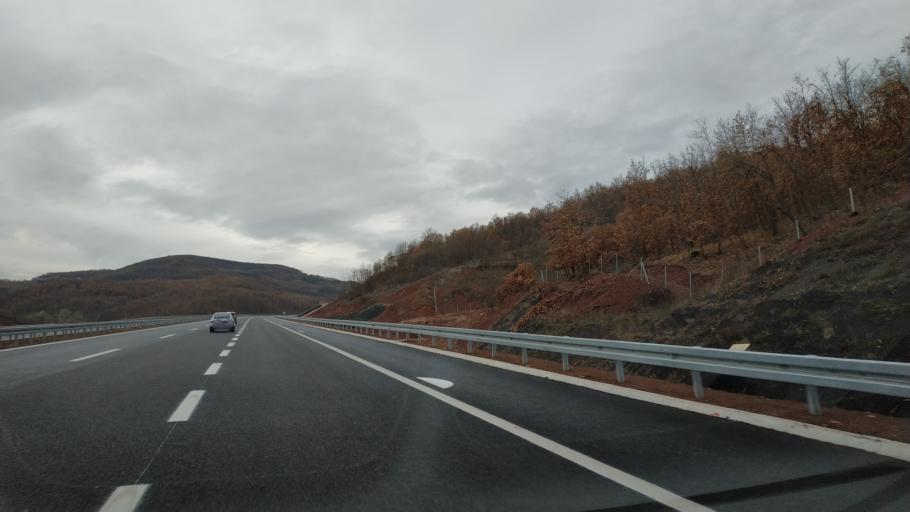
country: RS
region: Central Serbia
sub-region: Nisavski Okrug
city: Gadzin Han
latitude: 43.2568
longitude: 22.1538
